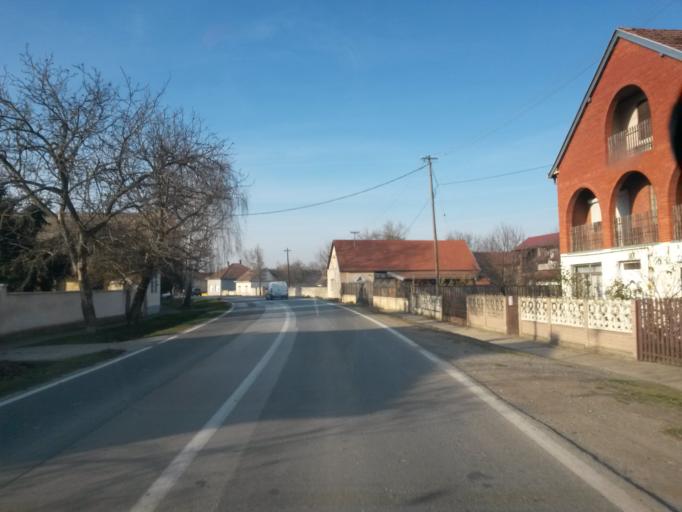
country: HR
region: Vukovarsko-Srijemska
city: Markusica
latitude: 45.3744
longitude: 18.7058
